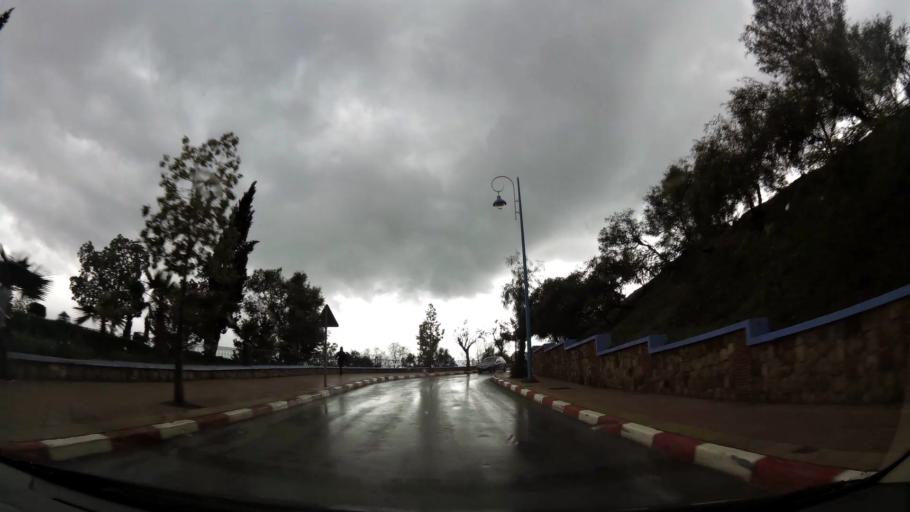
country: MA
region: Tanger-Tetouan
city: Chefchaouene
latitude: 35.1732
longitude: -5.2745
